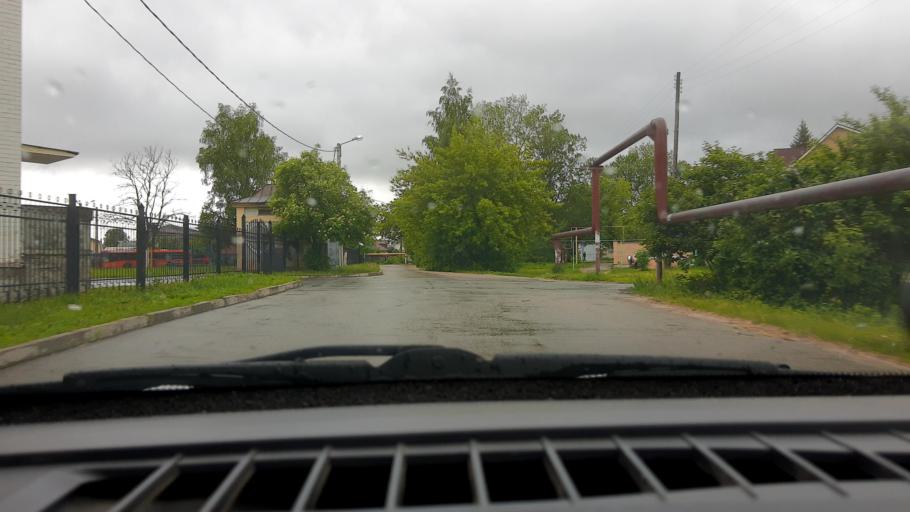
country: RU
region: Nizjnij Novgorod
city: Neklyudovo
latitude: 56.3626
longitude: 43.8463
